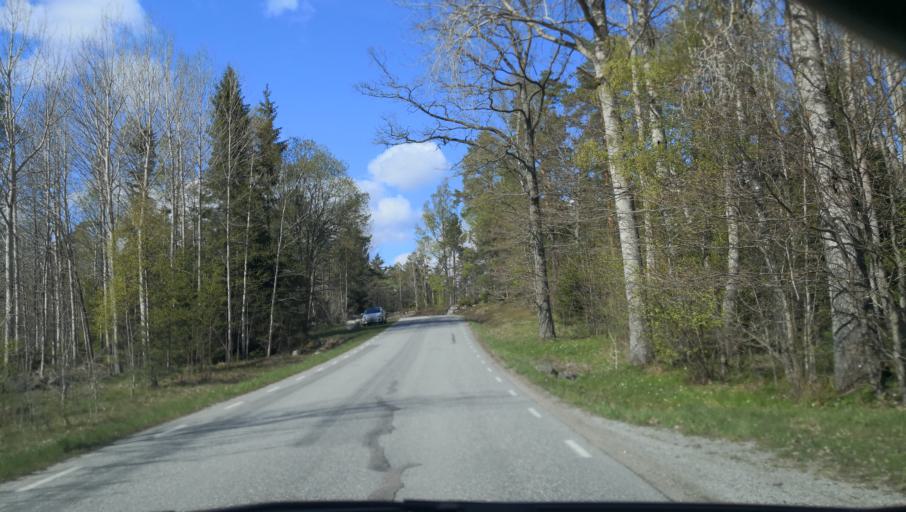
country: SE
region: Stockholm
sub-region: Varmdo Kommun
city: Hemmesta
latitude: 59.3953
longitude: 18.5115
